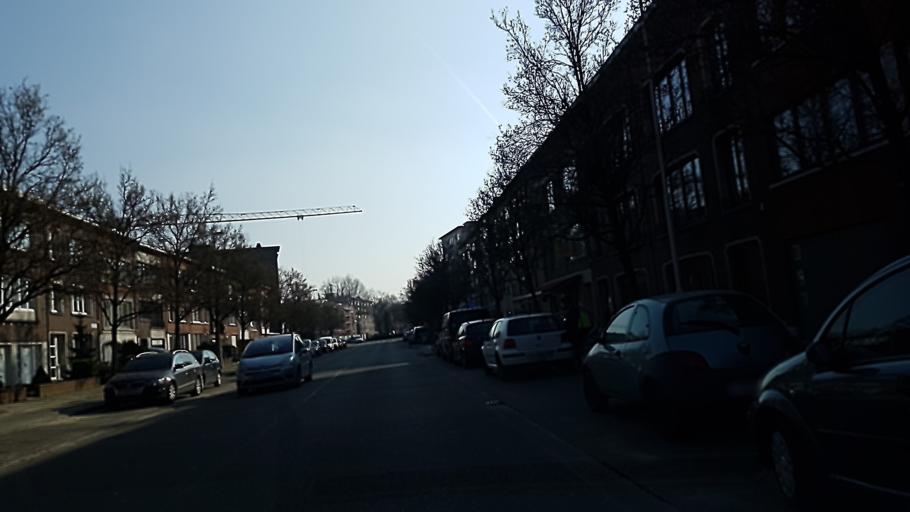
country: BE
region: Flanders
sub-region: Provincie Antwerpen
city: Mortsel
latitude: 51.1990
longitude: 4.4498
